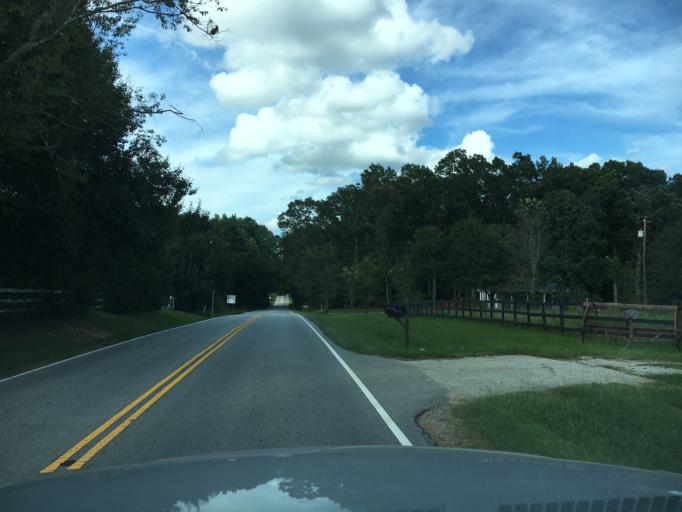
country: US
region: South Carolina
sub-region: Greenville County
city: Fountain Inn
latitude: 34.7067
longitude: -82.1785
